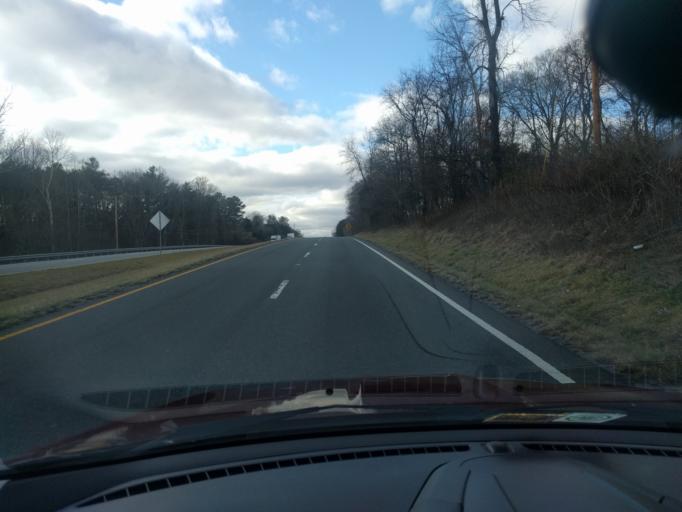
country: US
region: Virginia
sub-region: City of Bedford
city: Bedford
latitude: 37.3520
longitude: -79.6452
